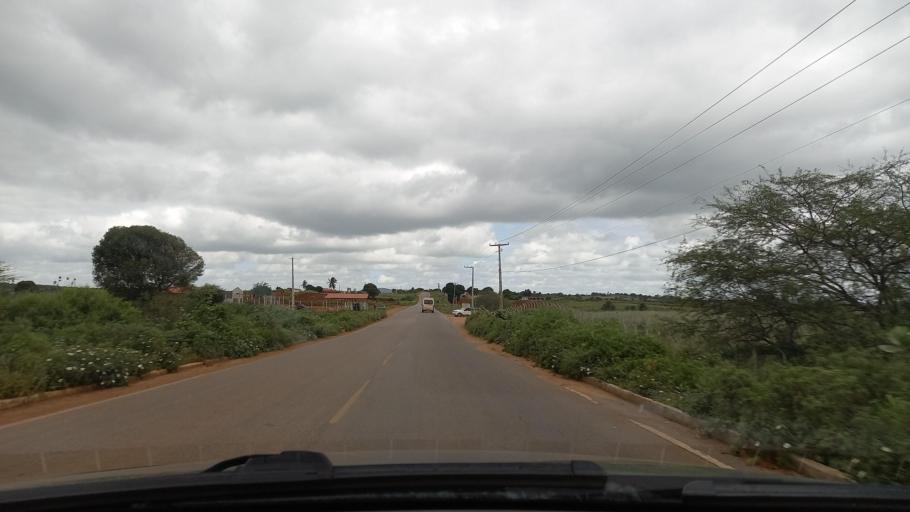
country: BR
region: Sergipe
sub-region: Caninde De Sao Francisco
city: Caninde de Sao Francisco
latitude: -9.6727
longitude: -37.8001
